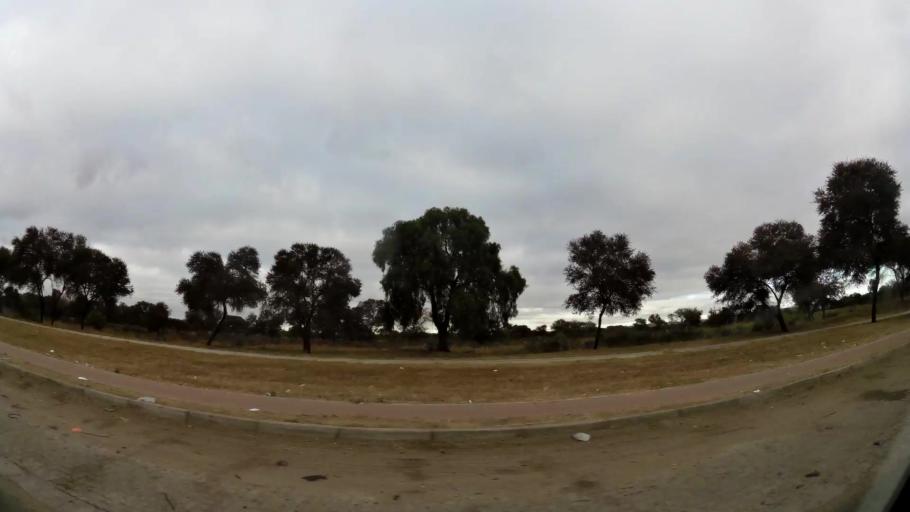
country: ZA
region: Limpopo
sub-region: Capricorn District Municipality
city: Polokwane
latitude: -23.8986
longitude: 29.4391
